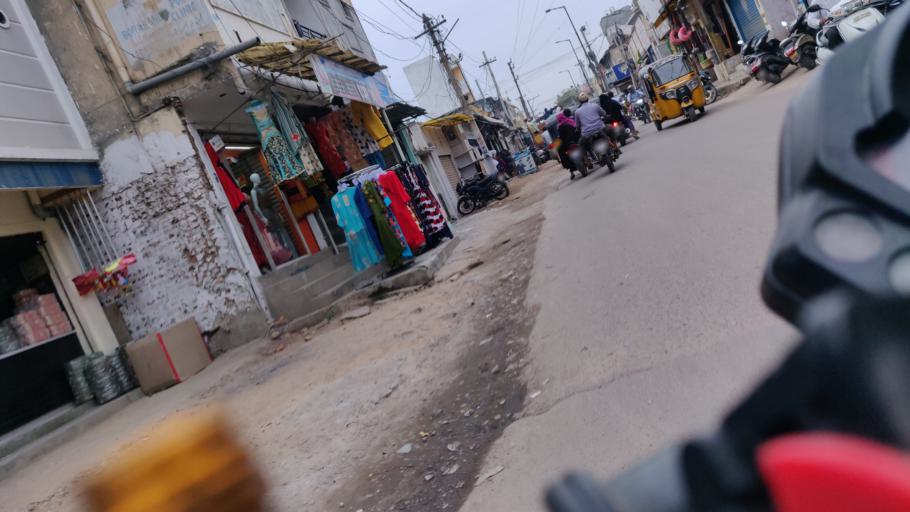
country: IN
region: Telangana
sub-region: Rangareddi
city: Kukatpalli
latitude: 17.4537
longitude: 78.4122
